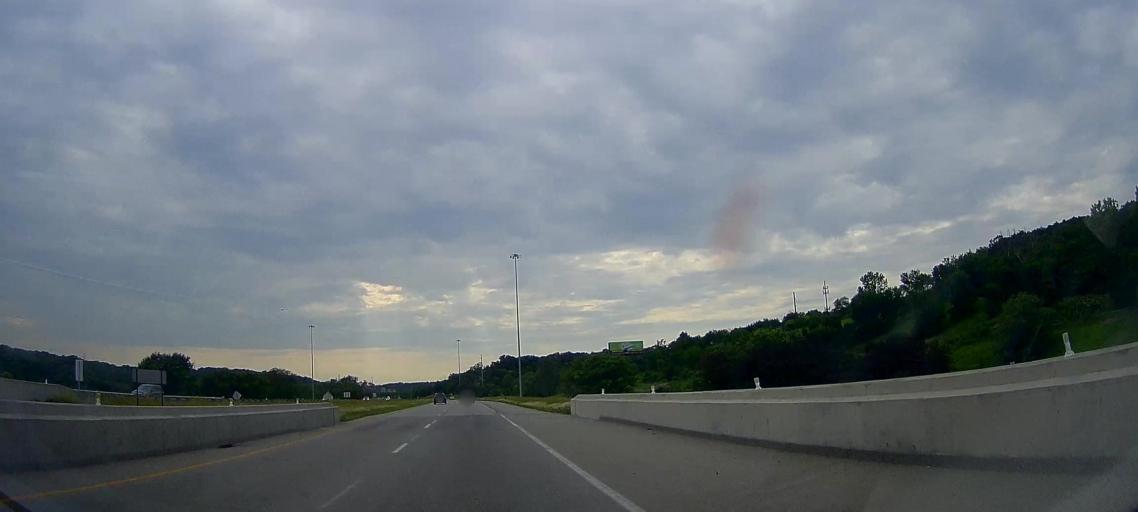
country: US
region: Iowa
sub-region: Pottawattamie County
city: Carter Lake
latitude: 41.3473
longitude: -95.9825
